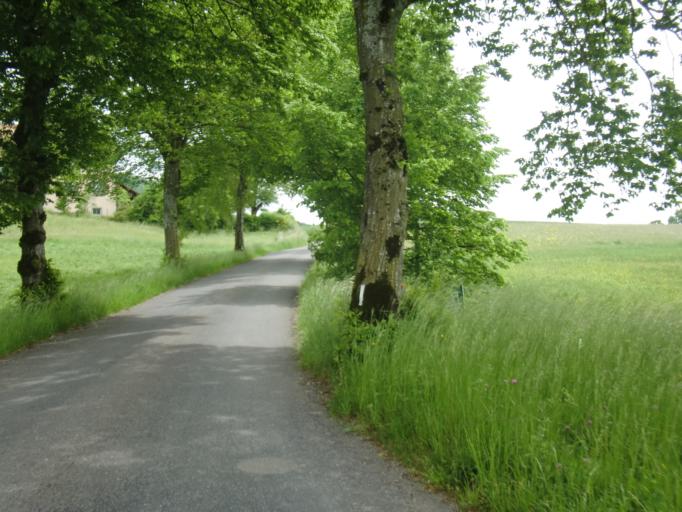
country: CH
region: Zurich
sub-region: Bezirk Hinwil
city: Hinwil
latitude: 47.2866
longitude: 8.8464
